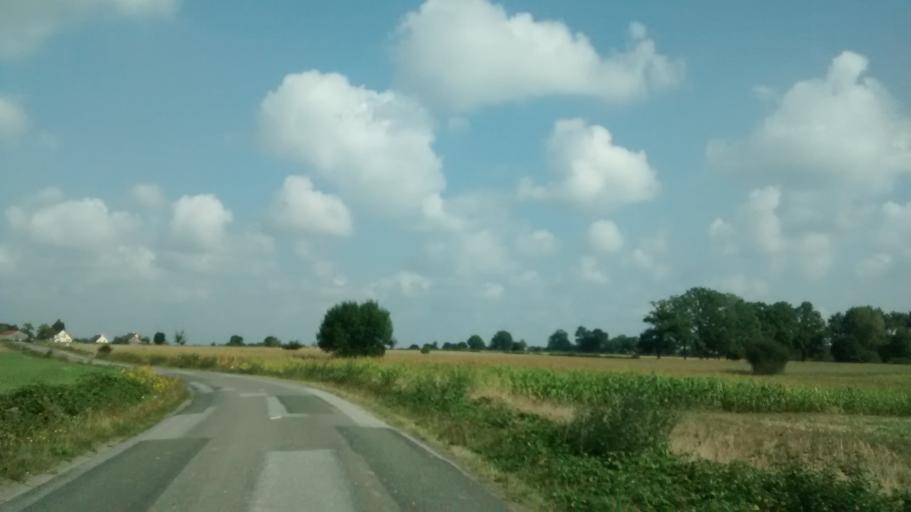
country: FR
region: Brittany
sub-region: Departement d'Ille-et-Vilaine
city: Erbree
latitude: 48.1307
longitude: -1.1010
